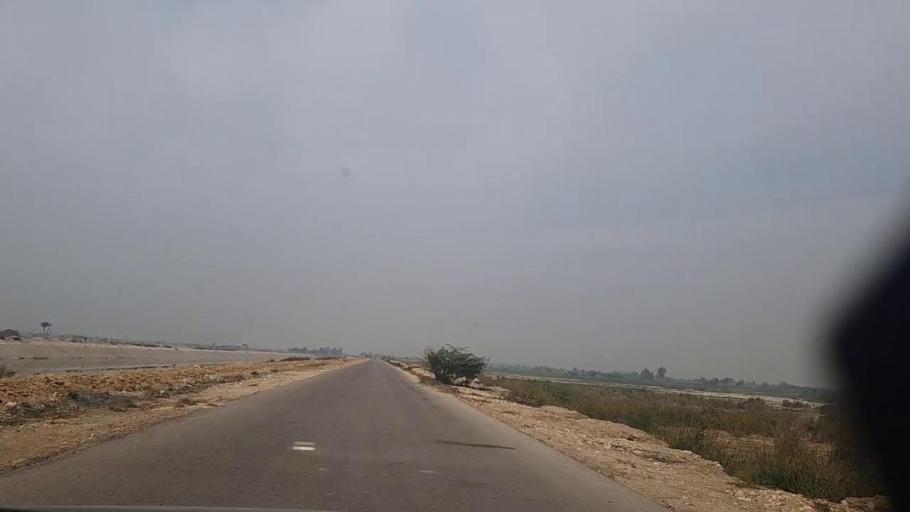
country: PK
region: Sindh
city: Sakrand
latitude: 26.2727
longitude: 68.2338
